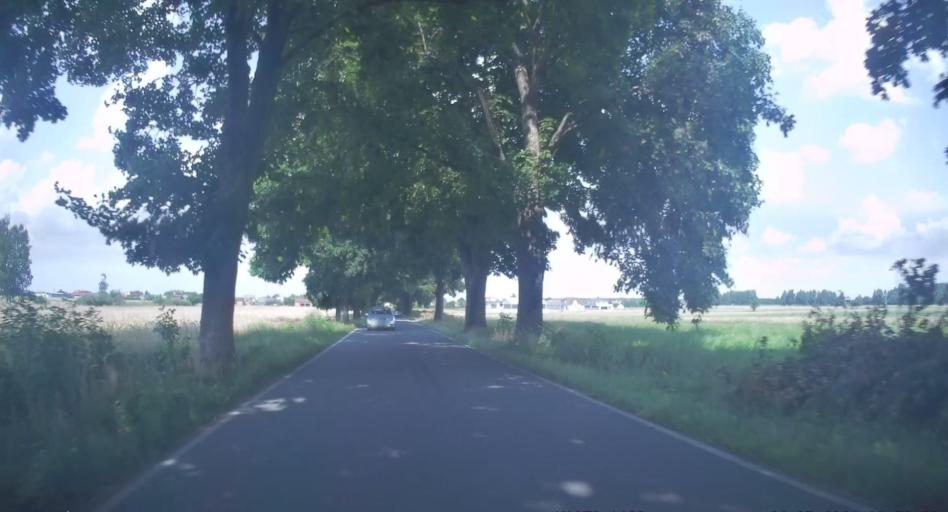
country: PL
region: Lodz Voivodeship
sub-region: Powiat tomaszowski
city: Lubochnia
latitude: 51.5643
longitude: 20.1190
